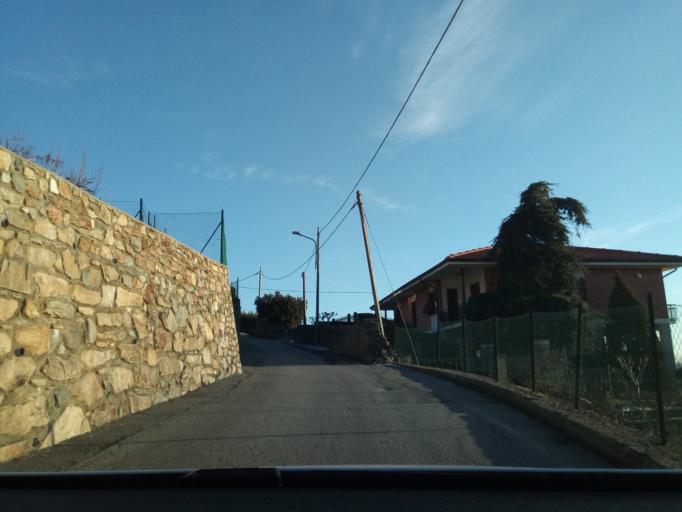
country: IT
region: Piedmont
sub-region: Provincia di Torino
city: Burolo
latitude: 45.4827
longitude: 7.9317
